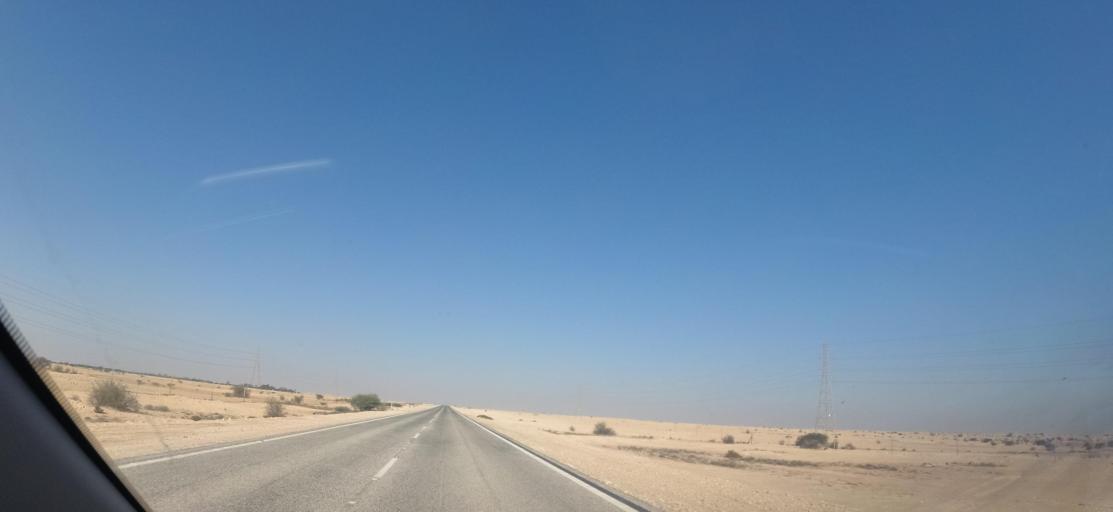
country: QA
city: Al Jumayliyah
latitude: 25.6577
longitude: 51.1175
